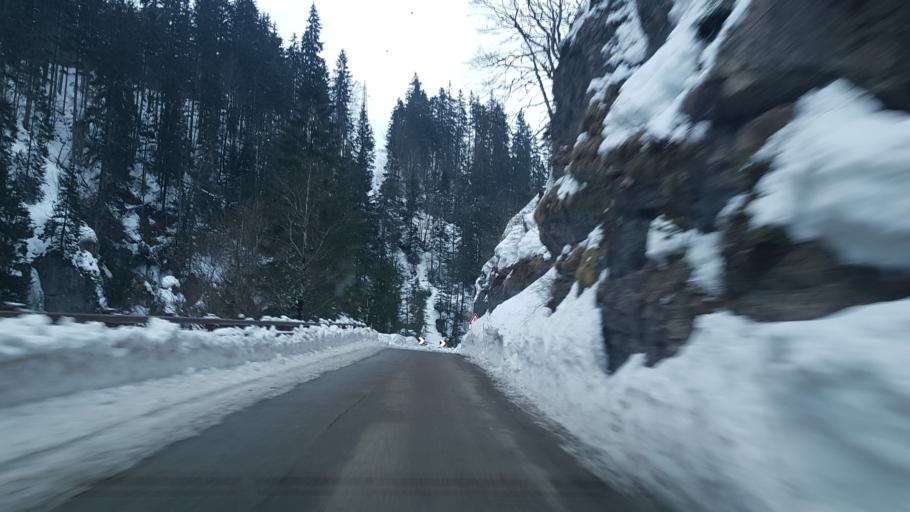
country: IT
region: Friuli Venezia Giulia
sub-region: Provincia di Udine
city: Malborghetto
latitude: 46.5250
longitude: 13.4738
